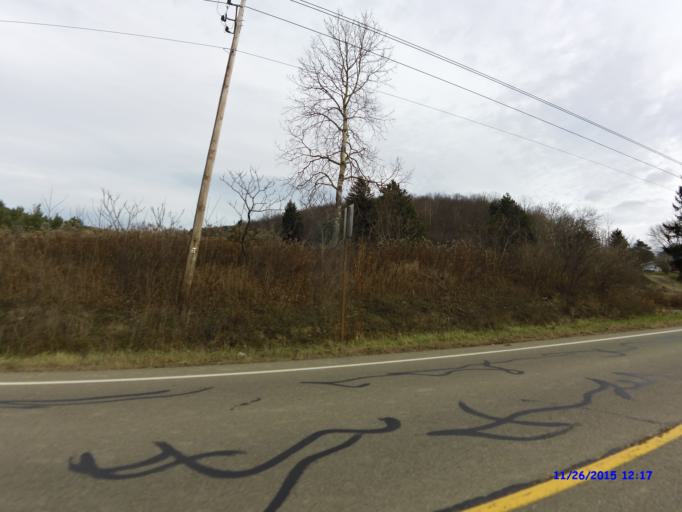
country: US
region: New York
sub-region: Cattaraugus County
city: Allegany
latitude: 42.1068
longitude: -78.4905
